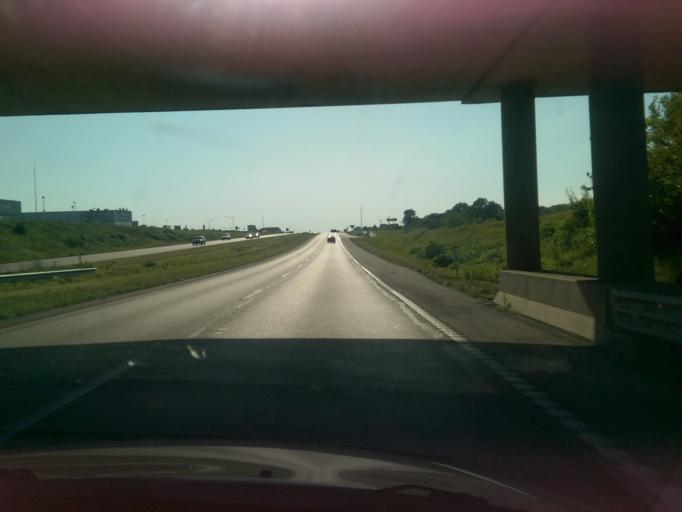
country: US
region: Missouri
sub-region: Lafayette County
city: Odessa
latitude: 39.0086
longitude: -93.9652
